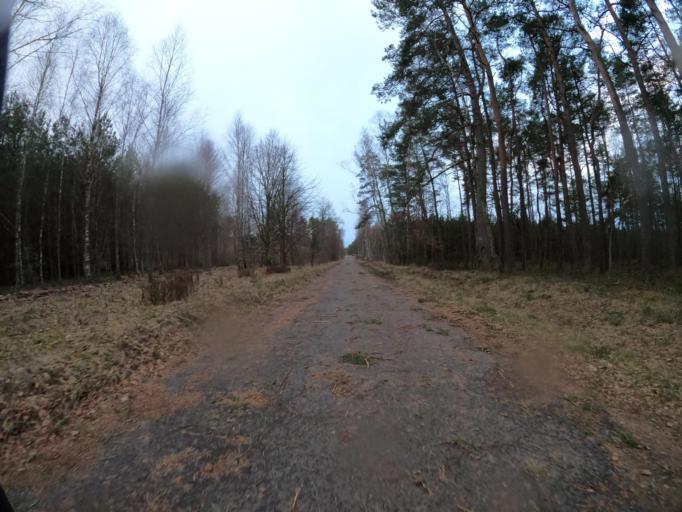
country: PL
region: West Pomeranian Voivodeship
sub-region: Powiat szczecinecki
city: Borne Sulinowo
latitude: 53.5535
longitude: 16.5795
